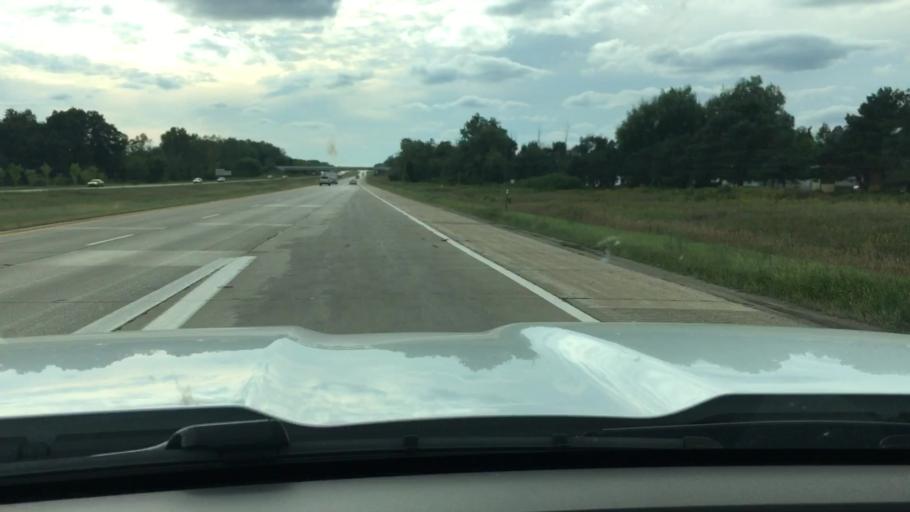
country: US
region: Michigan
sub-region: Lapeer County
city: Imlay City
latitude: 43.0005
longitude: -83.0760
